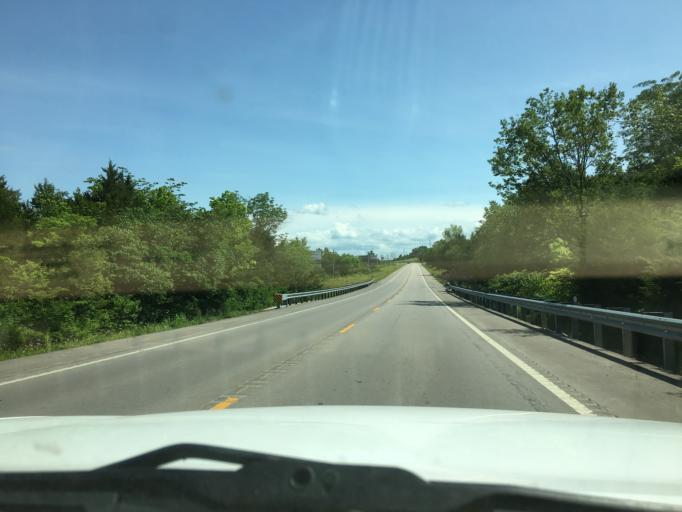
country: US
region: Missouri
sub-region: Franklin County
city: Union
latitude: 38.4665
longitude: -91.0054
